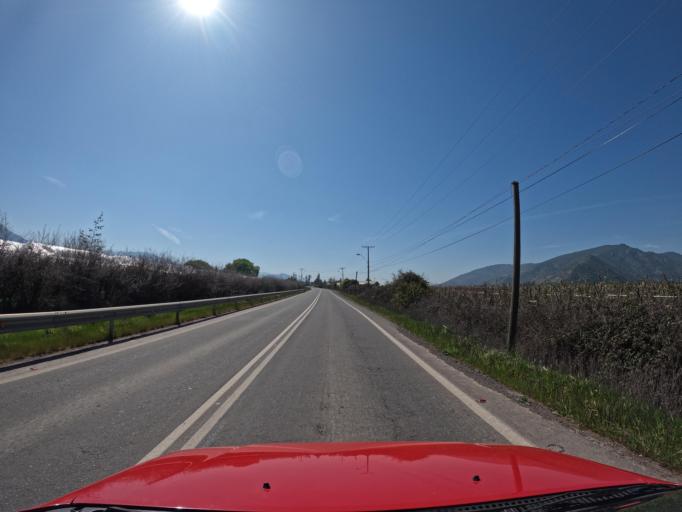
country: CL
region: Maule
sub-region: Provincia de Curico
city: Rauco
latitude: -35.0308
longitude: -71.4404
